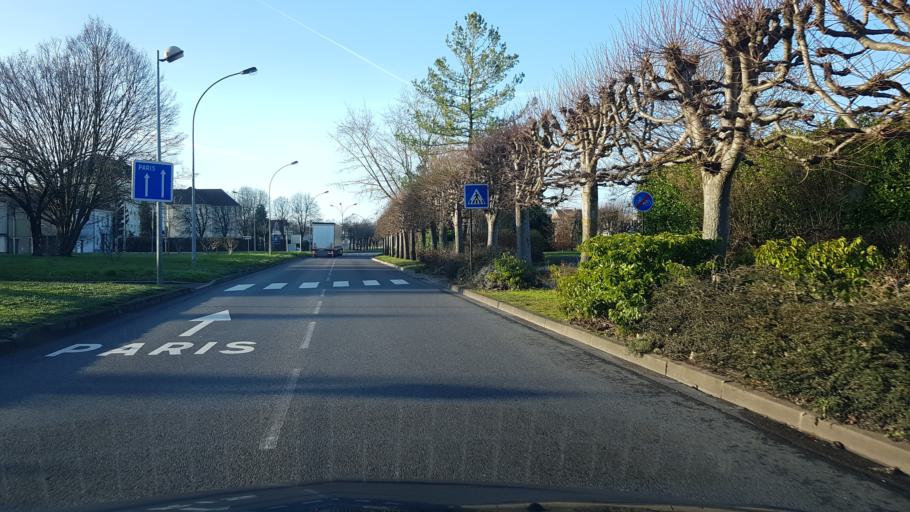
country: FR
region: Champagne-Ardenne
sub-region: Departement de la Marne
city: Vitry-le-Francois
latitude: 48.7291
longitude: 4.5870
